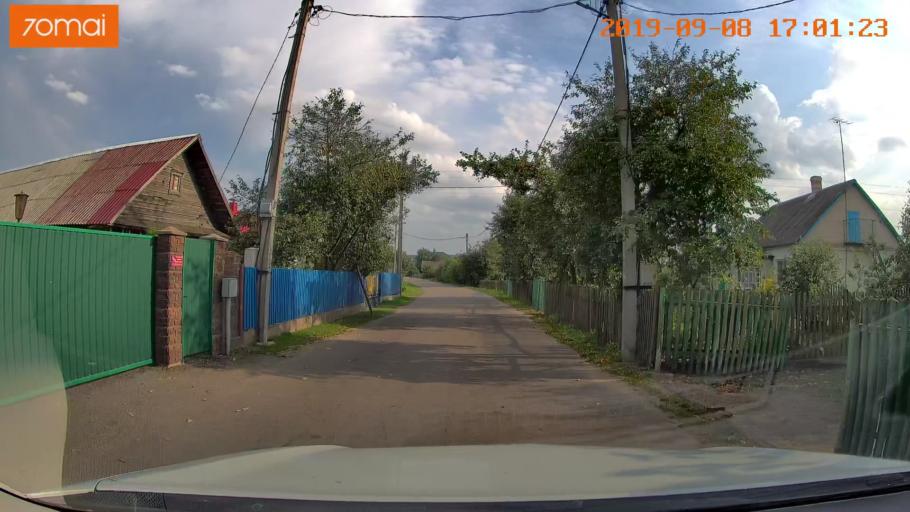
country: BY
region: Grodnenskaya
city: Hrodna
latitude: 53.7108
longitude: 23.9343
